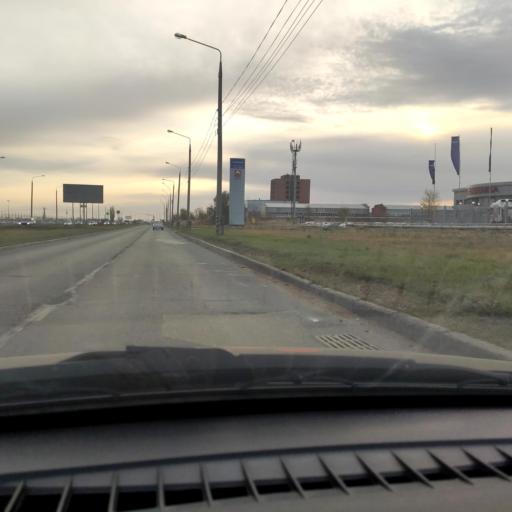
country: RU
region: Samara
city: Tol'yatti
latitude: 53.5567
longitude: 49.3395
